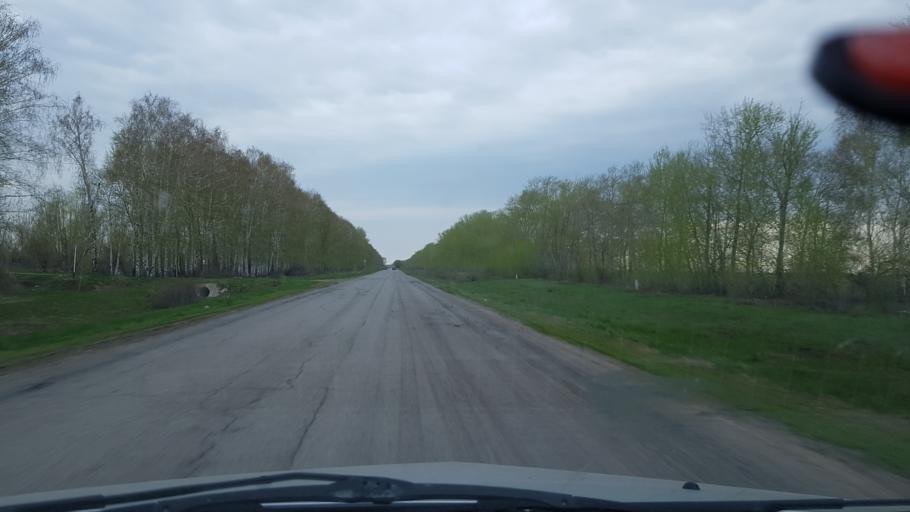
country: RU
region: Samara
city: Podstepki
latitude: 53.6636
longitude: 49.1883
